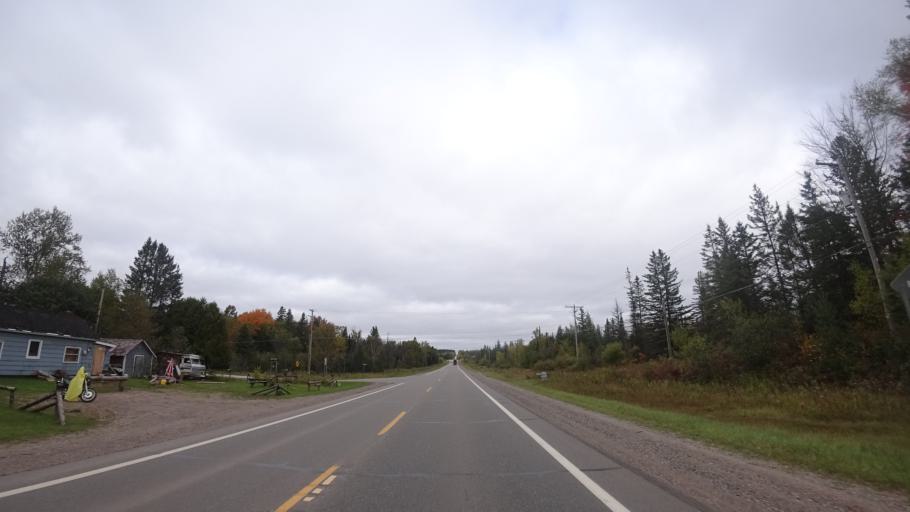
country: US
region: Wisconsin
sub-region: Florence County
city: Florence
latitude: 46.1013
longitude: -88.0757
